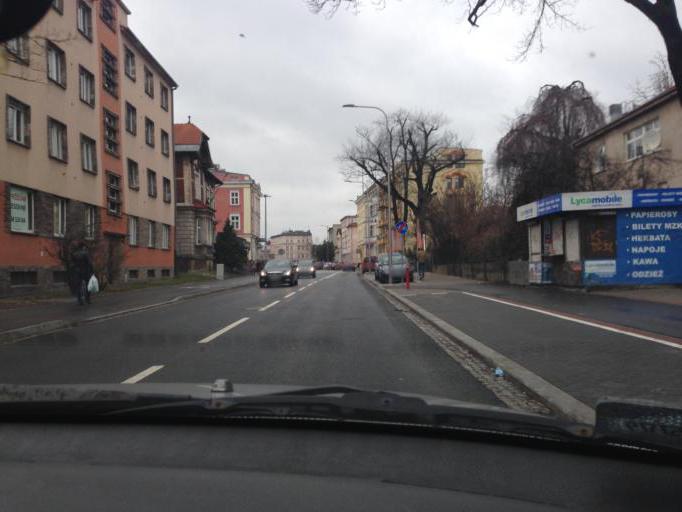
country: PL
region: Opole Voivodeship
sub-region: Powiat opolski
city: Opole
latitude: 50.6722
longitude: 17.9277
